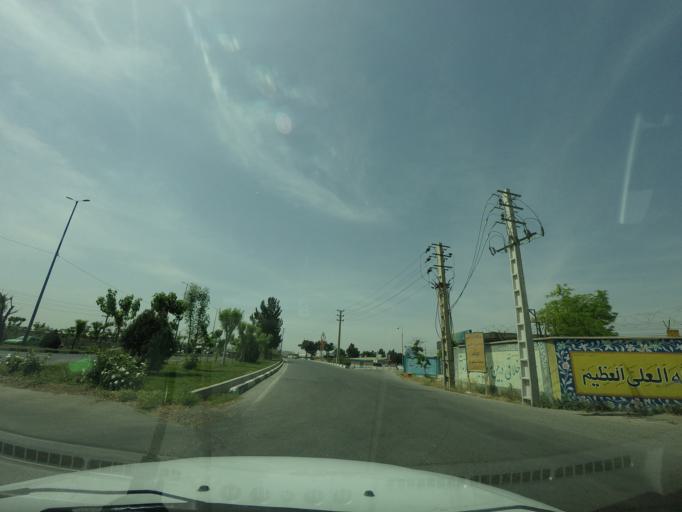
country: IR
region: Tehran
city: Eslamshahr
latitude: 35.5801
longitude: 51.2692
